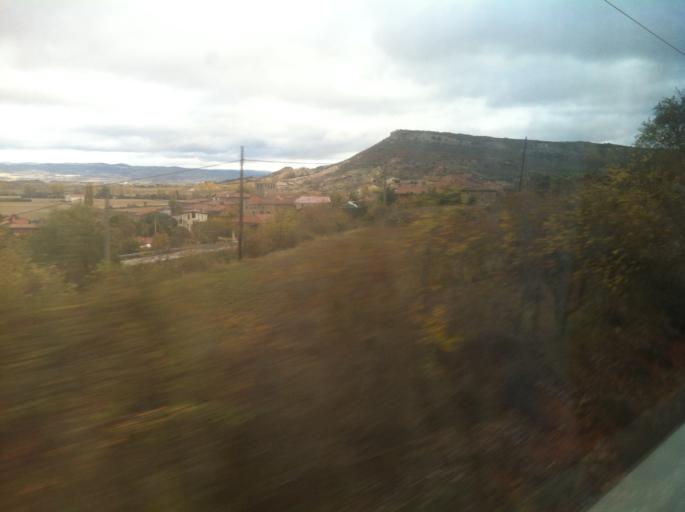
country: ES
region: Castille and Leon
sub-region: Provincia de Burgos
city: Bugedo
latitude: 42.6471
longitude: -3.0199
